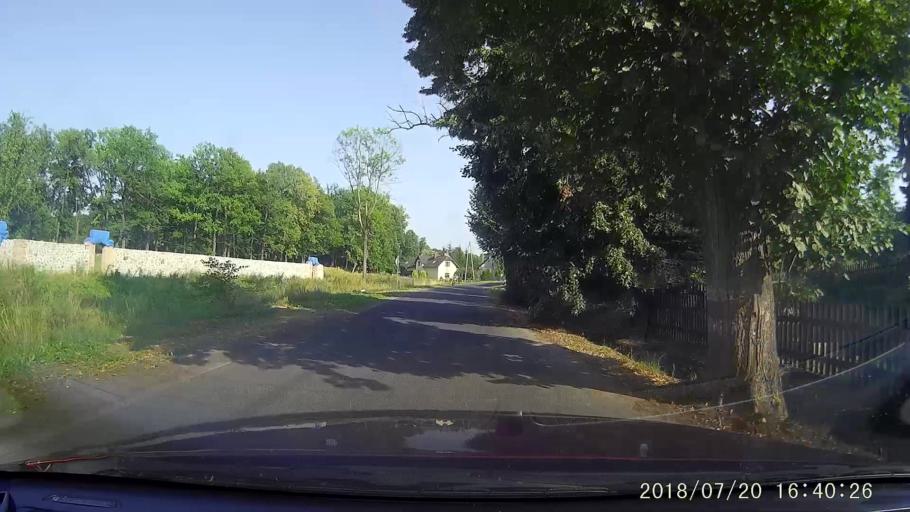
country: PL
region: Lower Silesian Voivodeship
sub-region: Powiat lubanski
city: Siekierczyn
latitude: 51.0858
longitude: 15.1467
